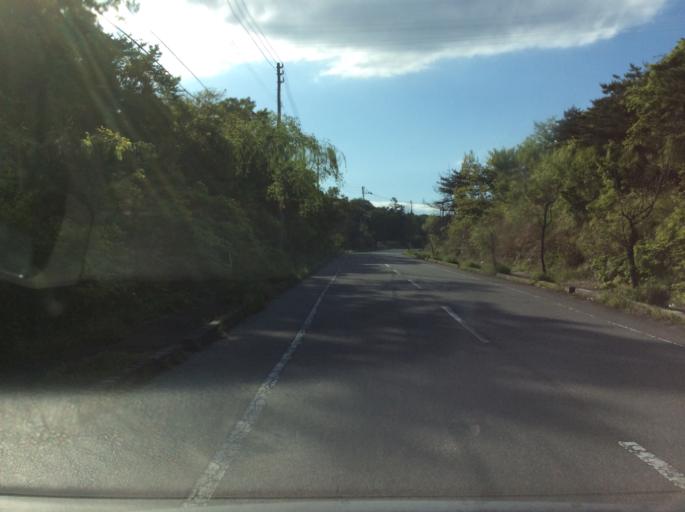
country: JP
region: Fukushima
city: Iwaki
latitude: 36.9639
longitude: 140.8485
